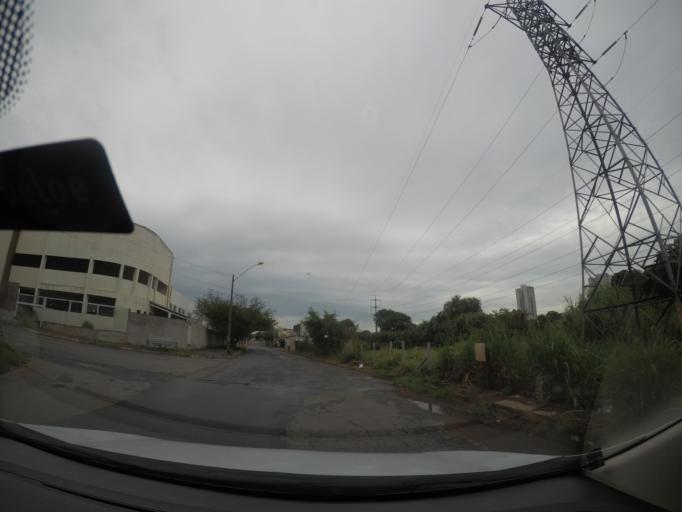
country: BR
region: Goias
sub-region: Goiania
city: Goiania
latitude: -16.6505
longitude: -49.2627
